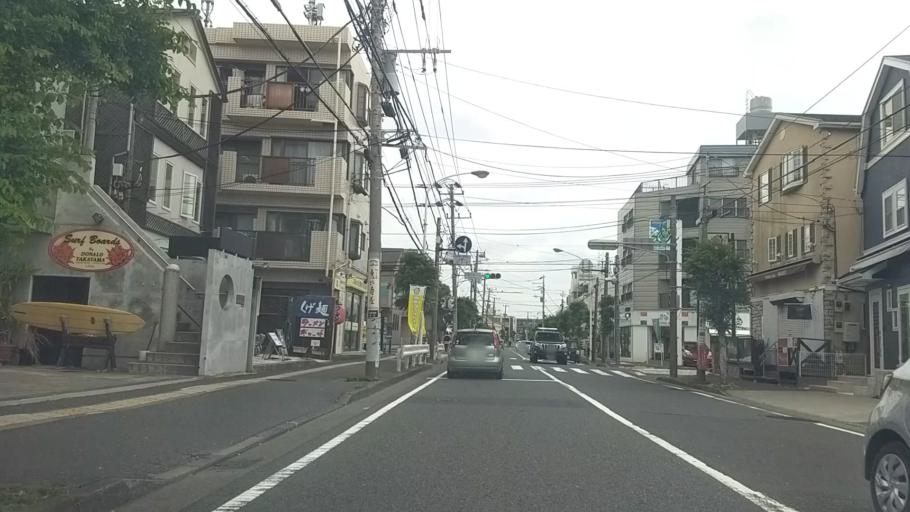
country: JP
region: Kanagawa
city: Fujisawa
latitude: 35.3267
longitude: 139.4674
